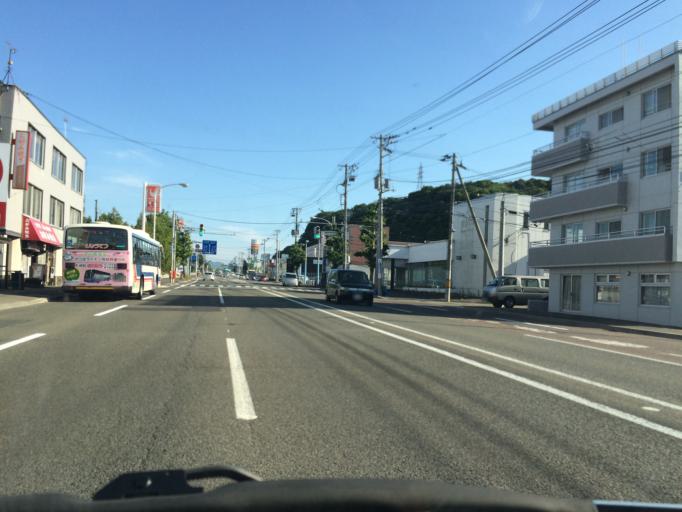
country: JP
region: Hokkaido
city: Sapporo
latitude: 43.0208
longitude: 141.3462
